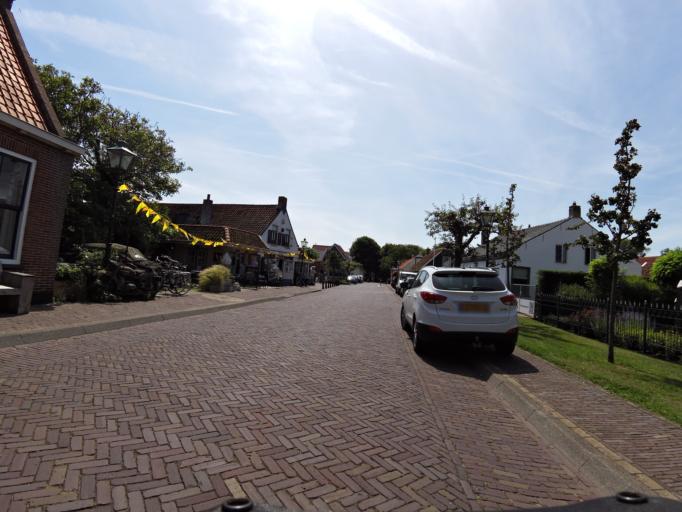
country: NL
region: Zeeland
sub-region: Schouwen-Duiveland
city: Burgh
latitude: 51.6905
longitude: 3.7318
